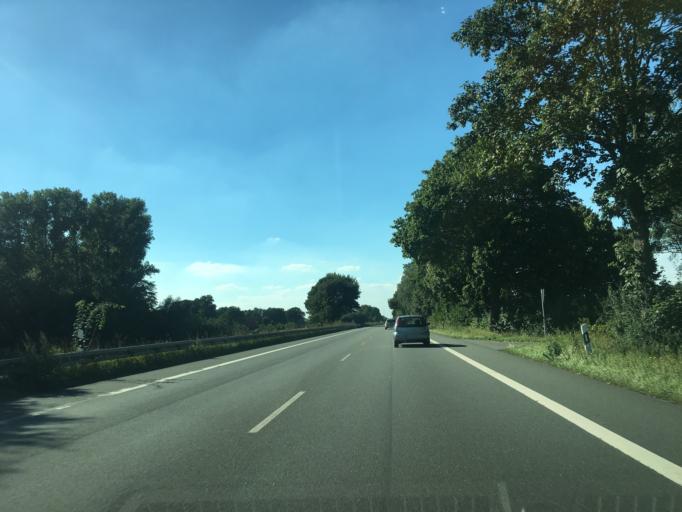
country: DE
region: North Rhine-Westphalia
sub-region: Regierungsbezirk Munster
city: Beelen
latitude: 51.9083
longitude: 8.1780
